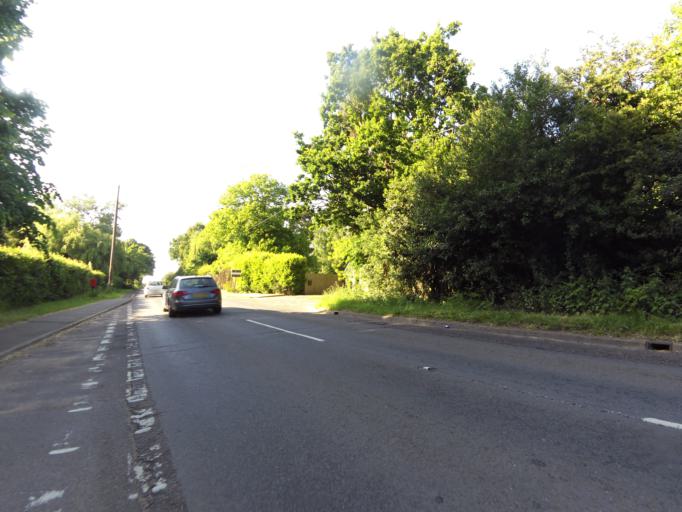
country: GB
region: England
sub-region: Suffolk
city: Woodbridge
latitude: 52.0957
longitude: 1.3496
